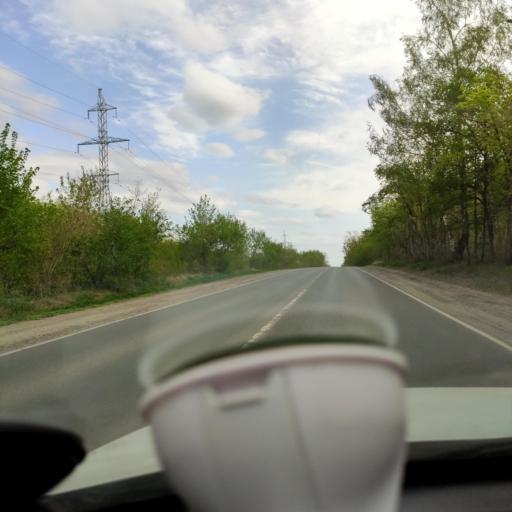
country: RU
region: Samara
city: Petra-Dubrava
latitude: 53.3190
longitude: 50.2677
